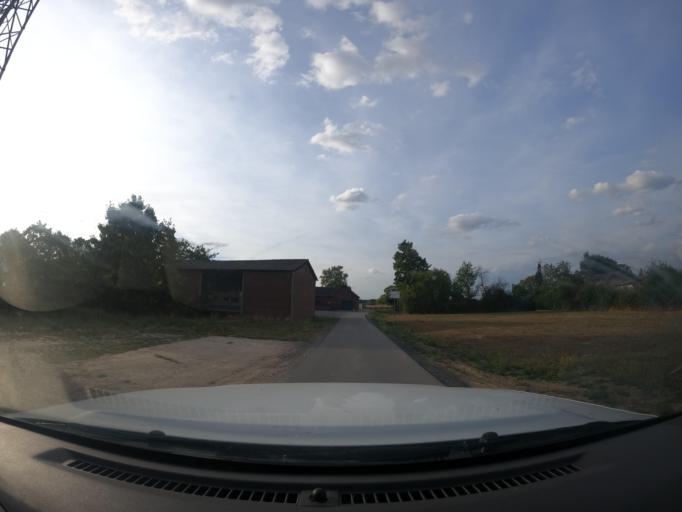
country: DE
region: North Rhine-Westphalia
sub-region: Regierungsbezirk Dusseldorf
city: Hamminkeln
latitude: 51.7033
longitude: 6.5855
